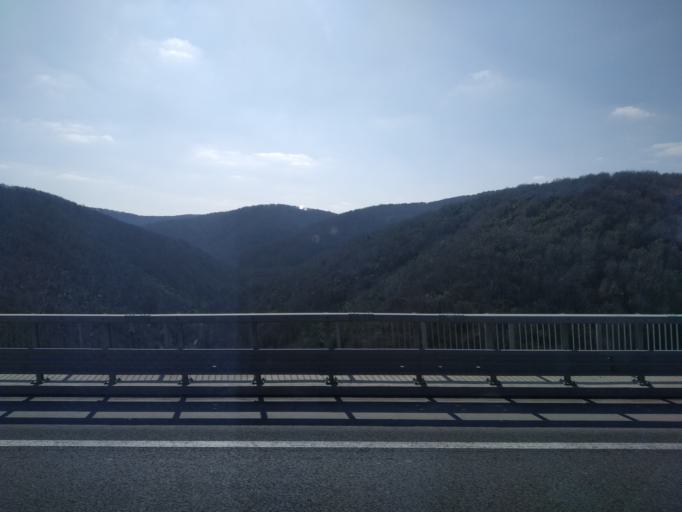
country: TR
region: Istanbul
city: Arikoey
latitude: 41.2322
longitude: 28.9654
